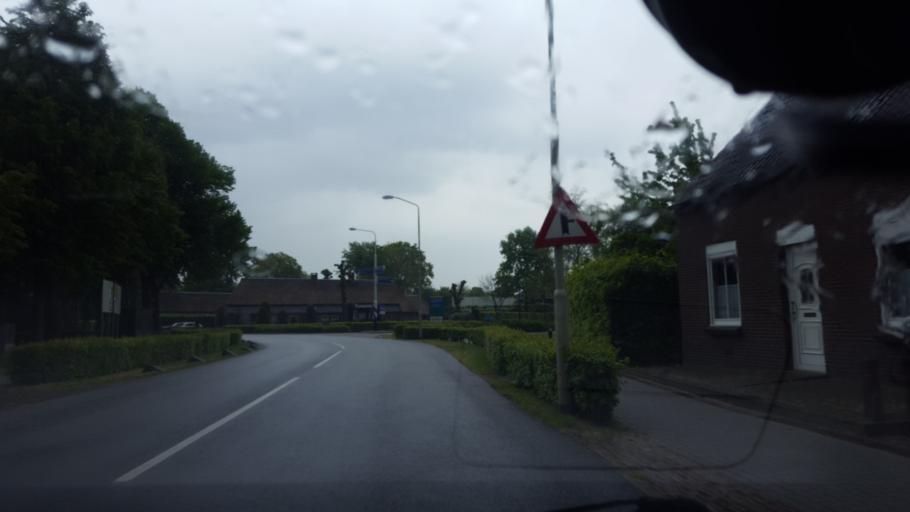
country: NL
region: North Brabant
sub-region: Gemeente Someren
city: Someren
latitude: 51.3650
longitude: 5.7310
